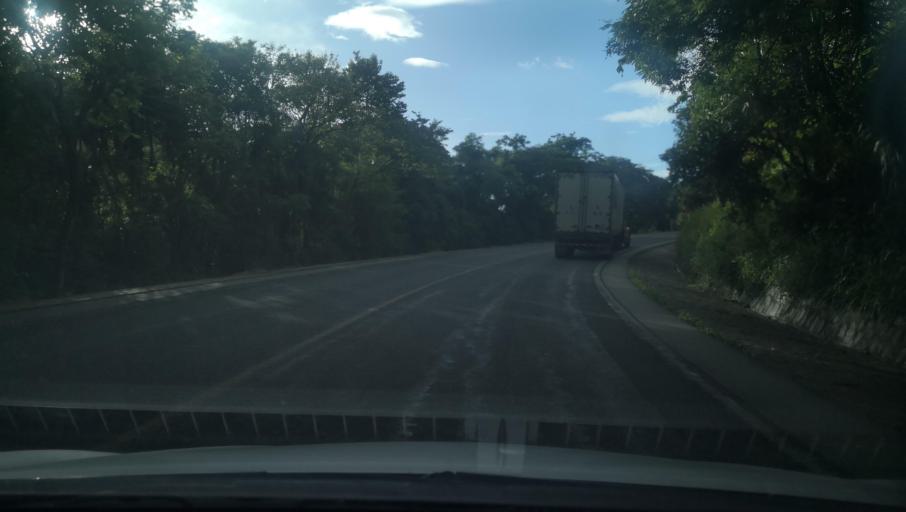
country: NI
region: Nueva Segovia
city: Mozonte
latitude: 13.7284
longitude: -86.5099
